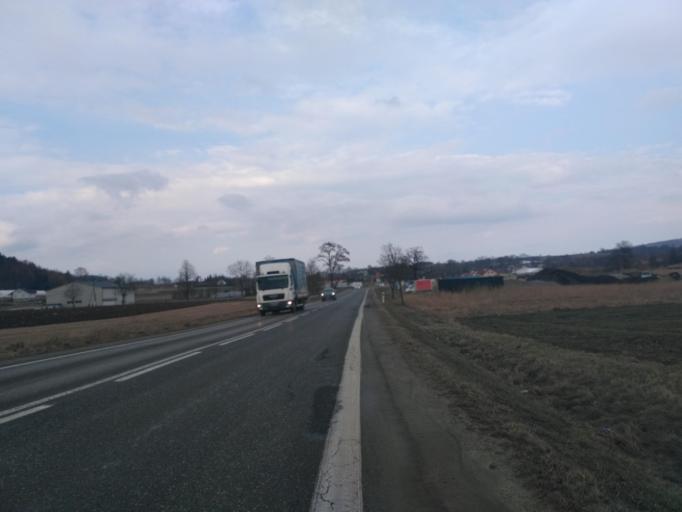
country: PL
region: Subcarpathian Voivodeship
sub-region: Powiat sanocki
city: Strachocina
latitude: 49.6097
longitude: 22.1193
